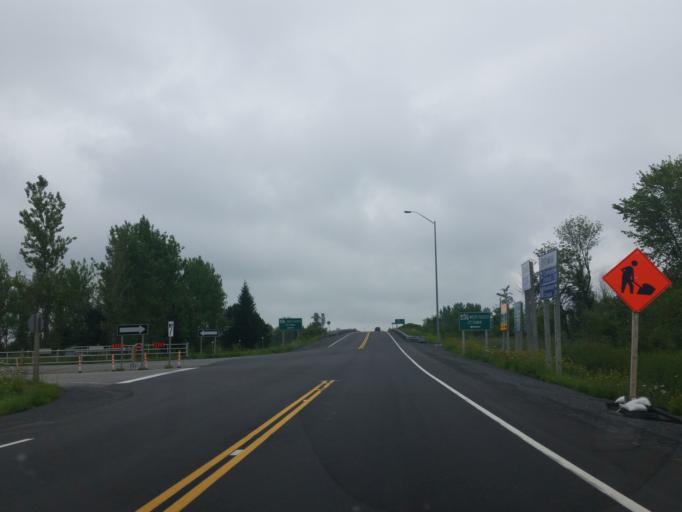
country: CA
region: Ontario
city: Bourget
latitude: 45.3386
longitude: -75.3446
